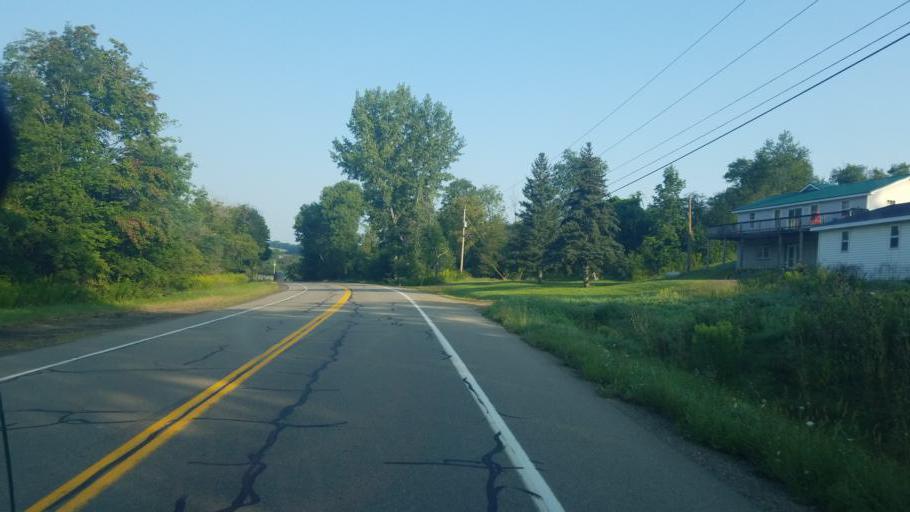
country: US
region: Pennsylvania
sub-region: Tioga County
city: Westfield
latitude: 42.0207
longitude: -77.5245
